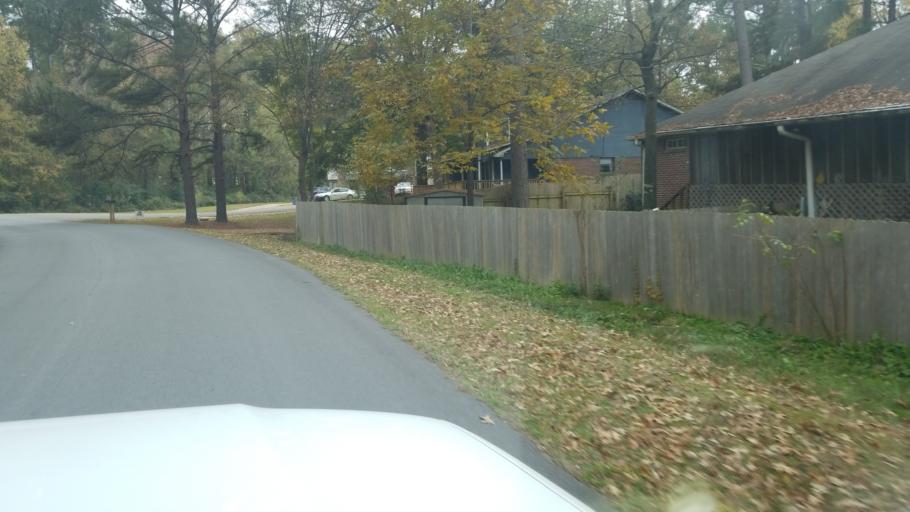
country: US
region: Mississippi
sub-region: Madison County
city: Ridgeland
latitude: 32.3826
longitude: -90.0331
